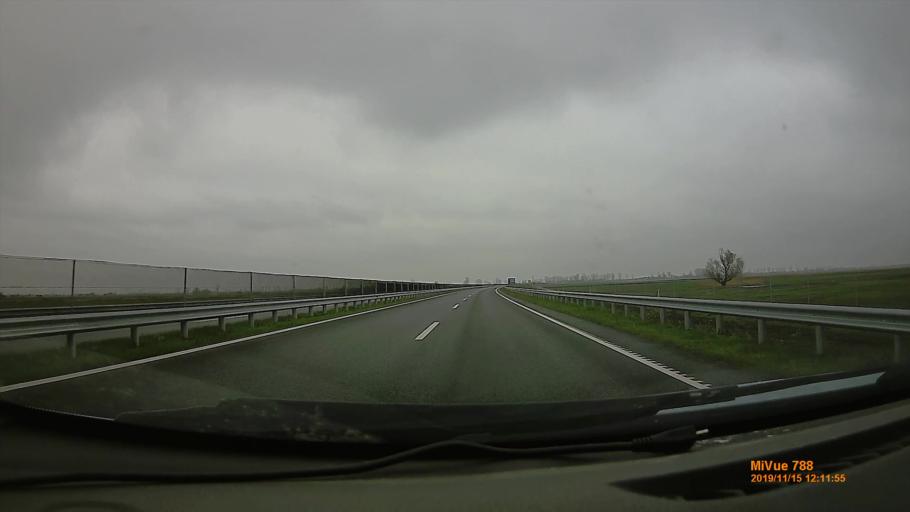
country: HU
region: Bekes
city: Bekesszentandras
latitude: 46.8253
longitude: 20.4583
